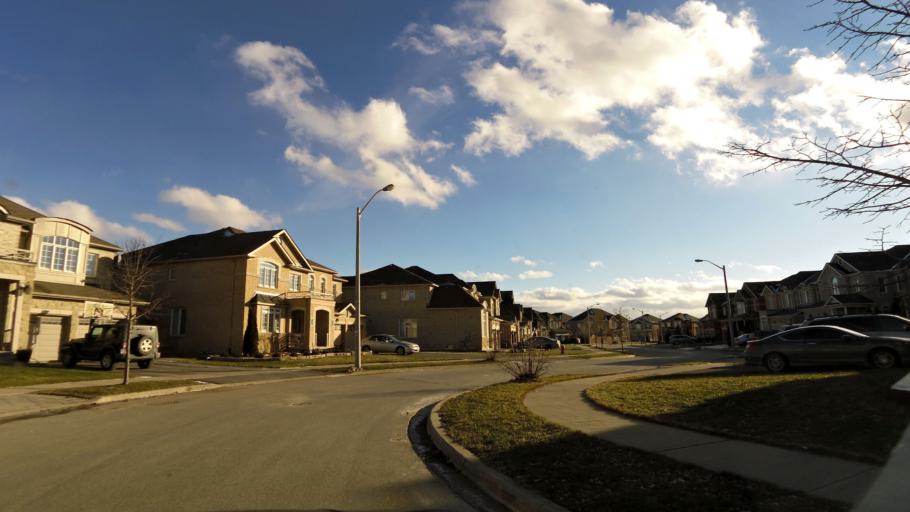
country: CA
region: Ontario
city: Brampton
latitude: 43.6371
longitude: -79.7700
